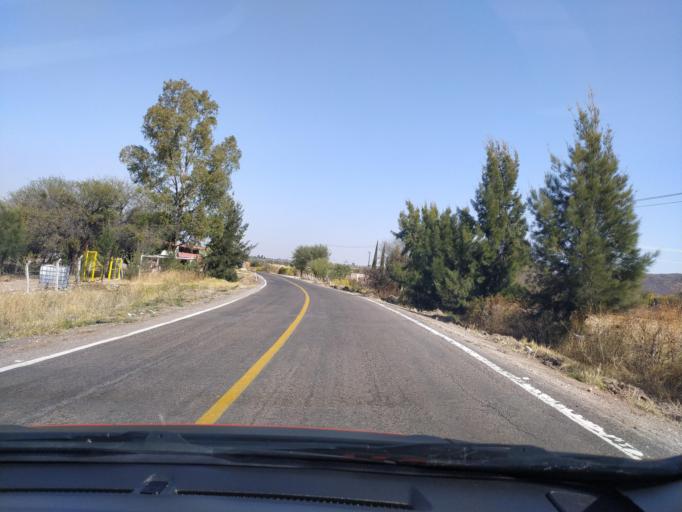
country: MX
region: Guanajuato
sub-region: San Francisco del Rincon
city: San Ignacio de Hidalgo
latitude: 20.8054
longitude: -101.8371
